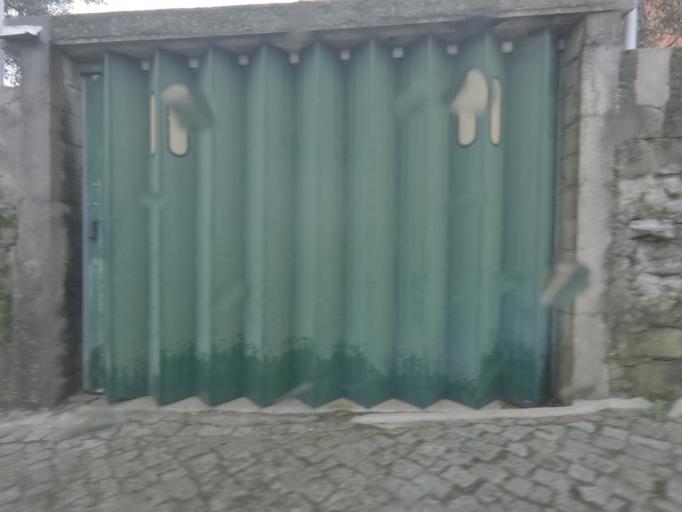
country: PT
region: Vila Real
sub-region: Peso da Regua
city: Peso da Regua
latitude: 41.1740
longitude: -7.7257
